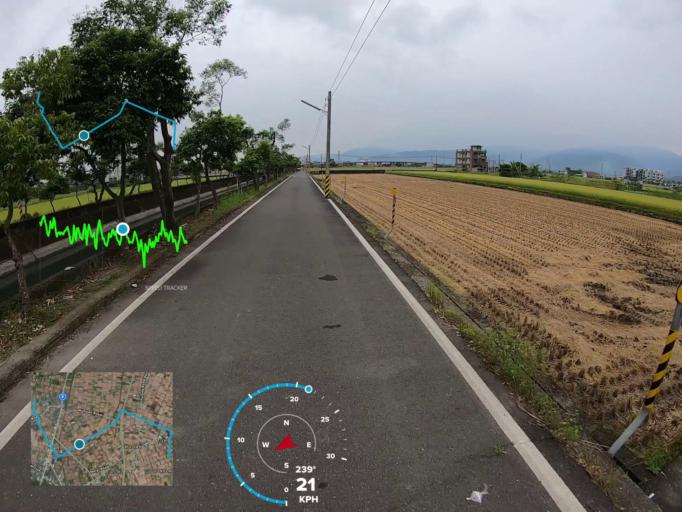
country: TW
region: Taiwan
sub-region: Yilan
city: Yilan
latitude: 24.7785
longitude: 121.7687
